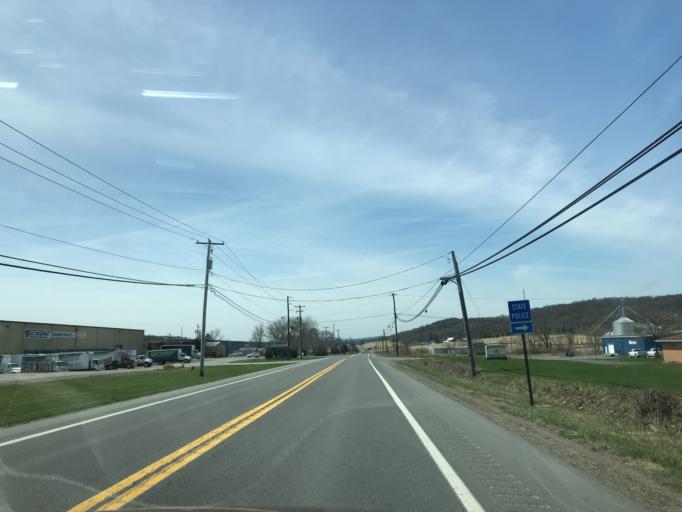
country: US
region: Pennsylvania
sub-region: Snyder County
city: Selinsgrove
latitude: 40.8058
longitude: -76.9116
